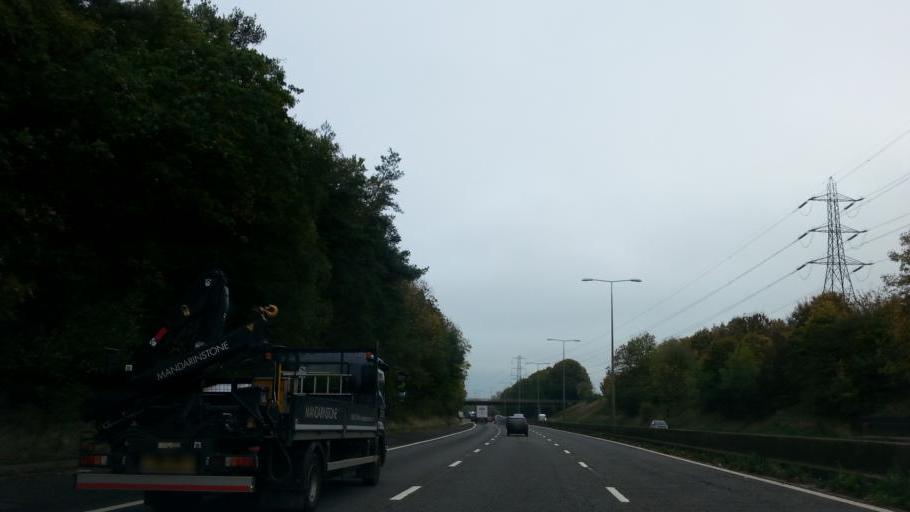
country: GB
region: England
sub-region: City and Borough of Birmingham
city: Bartley Green
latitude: 52.4106
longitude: -2.0285
